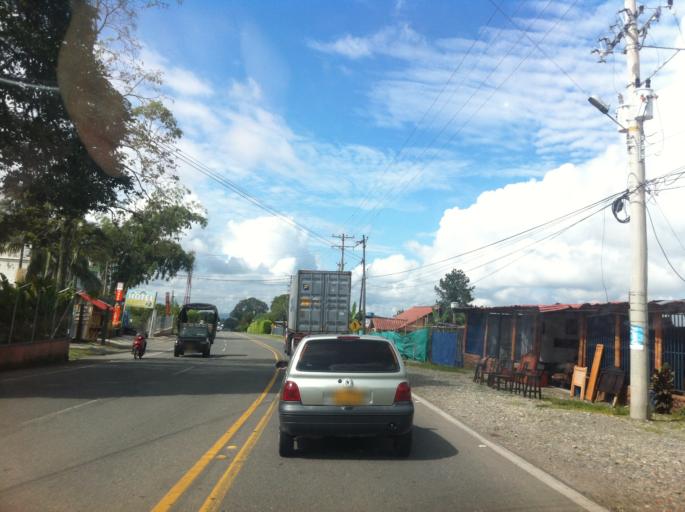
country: CO
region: Quindio
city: Armenia
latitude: 4.5002
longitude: -75.7245
